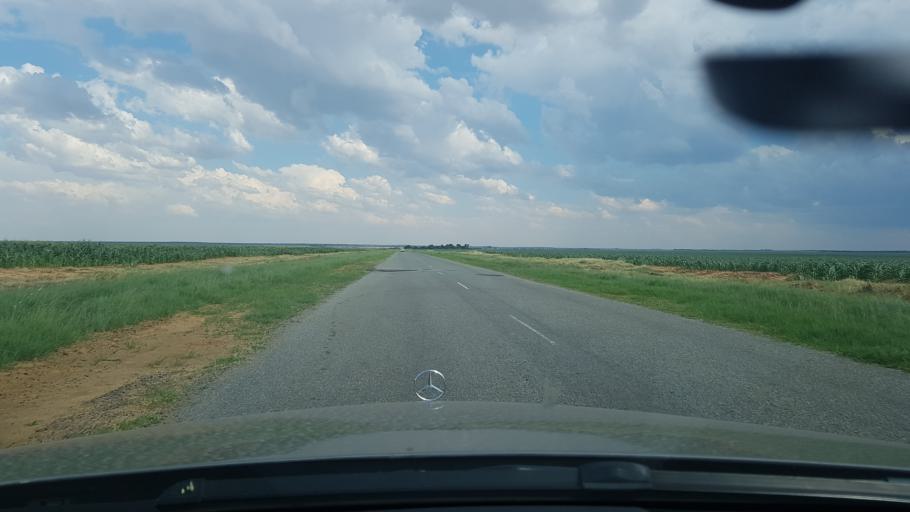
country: ZA
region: North-West
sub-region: Dr Ruth Segomotsi Mompati District Municipality
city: Bloemhof
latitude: -27.8165
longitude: 25.6286
